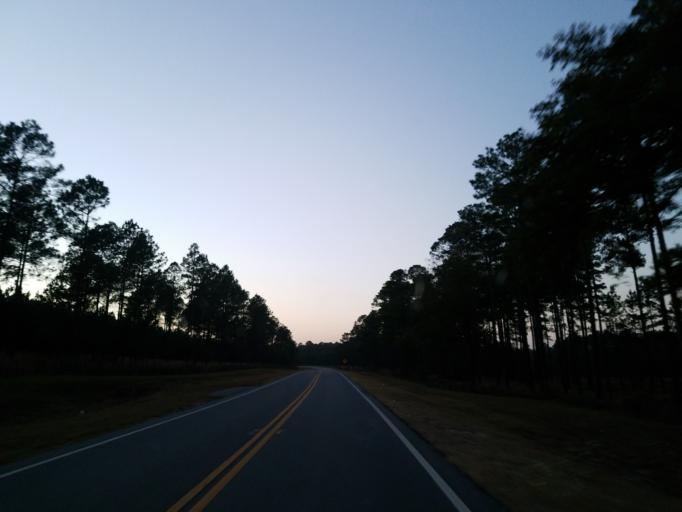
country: US
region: Georgia
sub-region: Wilcox County
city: Rochelle
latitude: 31.8223
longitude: -83.5446
